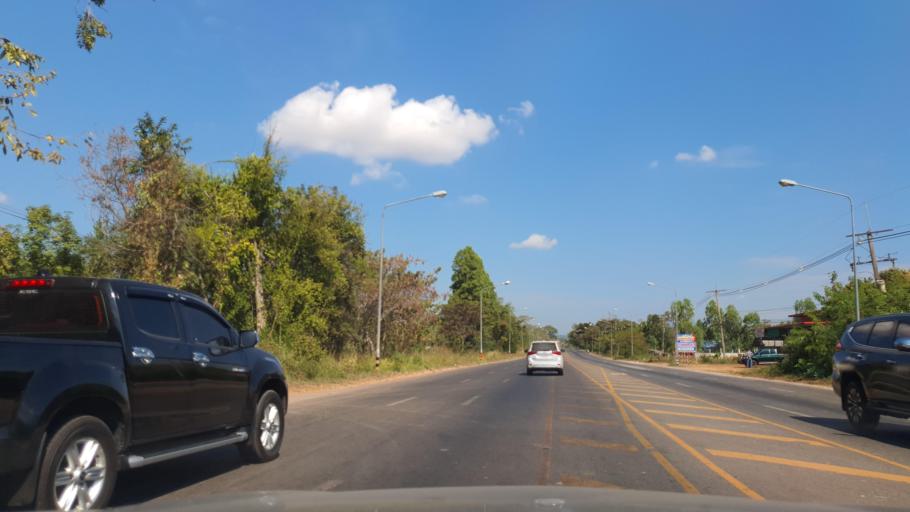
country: TH
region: Kalasin
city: Somdet
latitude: 16.7431
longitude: 103.7712
